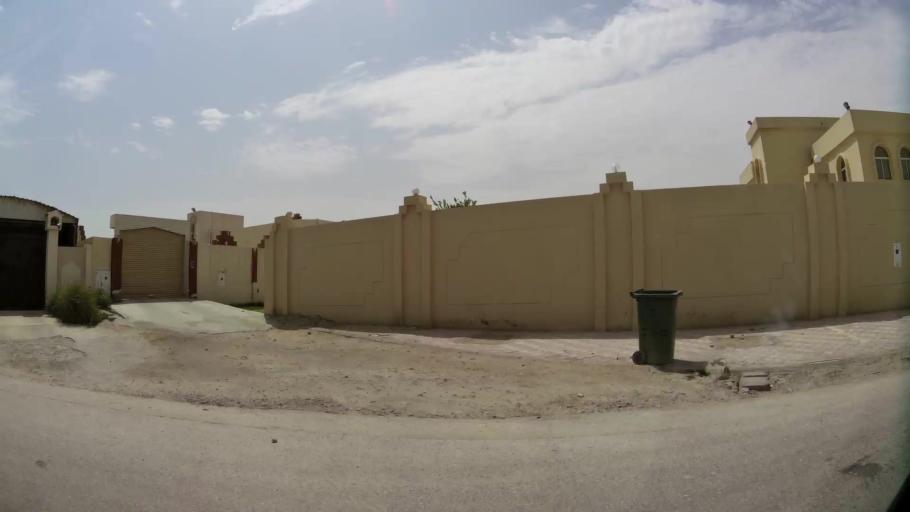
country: QA
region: Baladiyat ar Rayyan
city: Ar Rayyan
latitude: 25.3535
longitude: 51.4701
